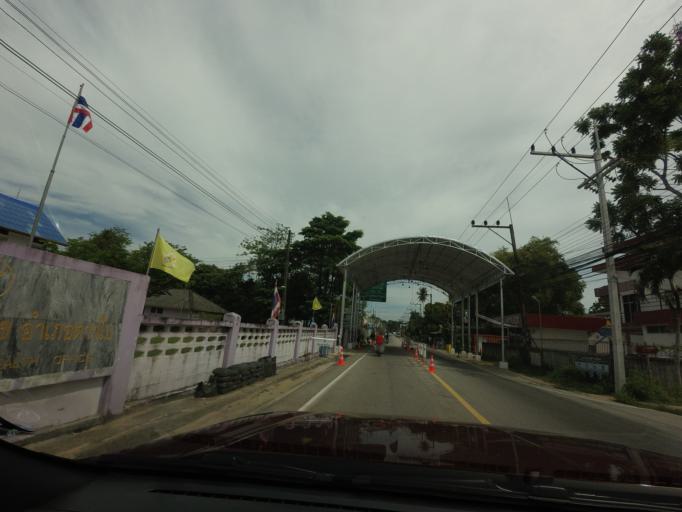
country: TH
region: Narathiwat
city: Tak Bai
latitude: 6.2579
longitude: 102.0550
